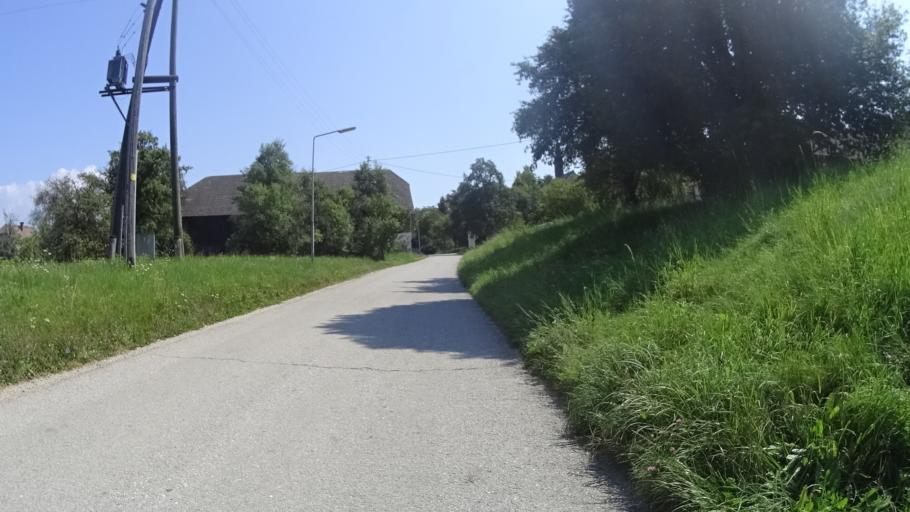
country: AT
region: Carinthia
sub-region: Politischer Bezirk Volkermarkt
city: Globasnitz
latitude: 46.5594
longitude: 14.6733
